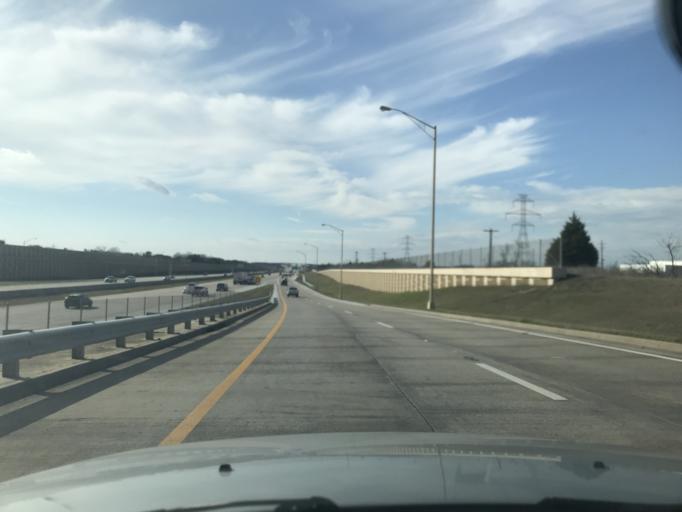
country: US
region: Texas
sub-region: Dallas County
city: Addison
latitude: 33.0129
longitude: -96.7986
